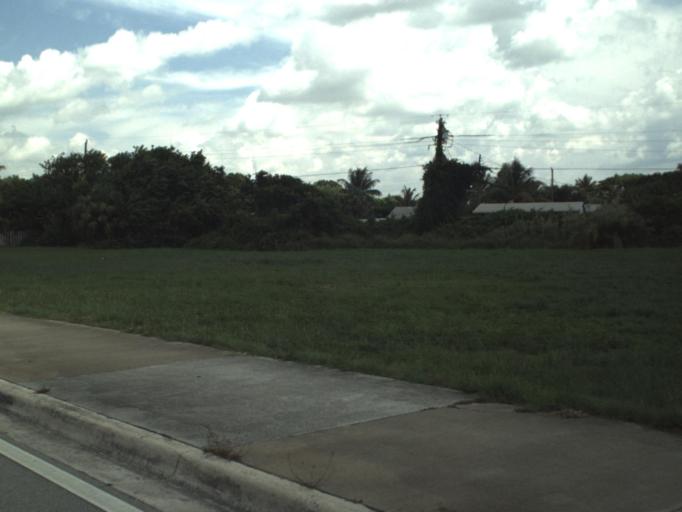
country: US
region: Florida
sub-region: Palm Beach County
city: North Palm Beach
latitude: 26.8141
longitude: -80.0788
